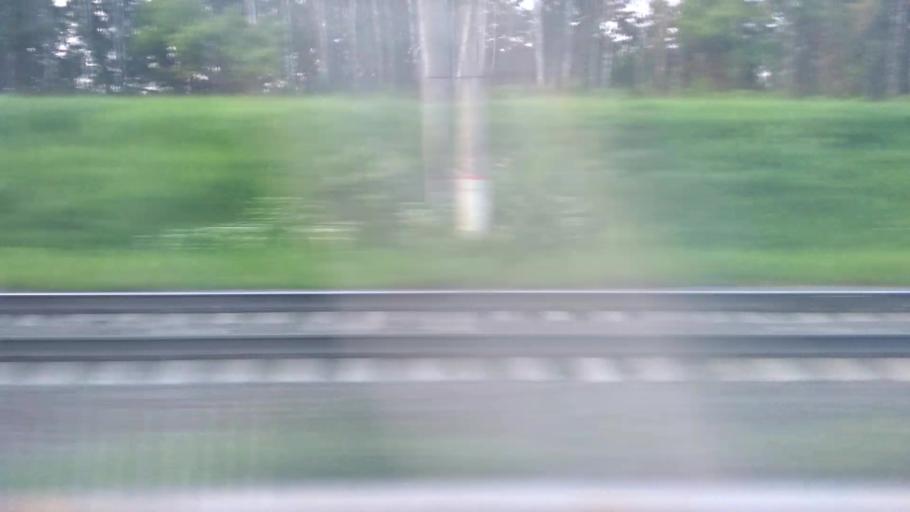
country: RU
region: Moskovskaya
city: Vostryakovo
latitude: 55.3779
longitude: 37.8180
